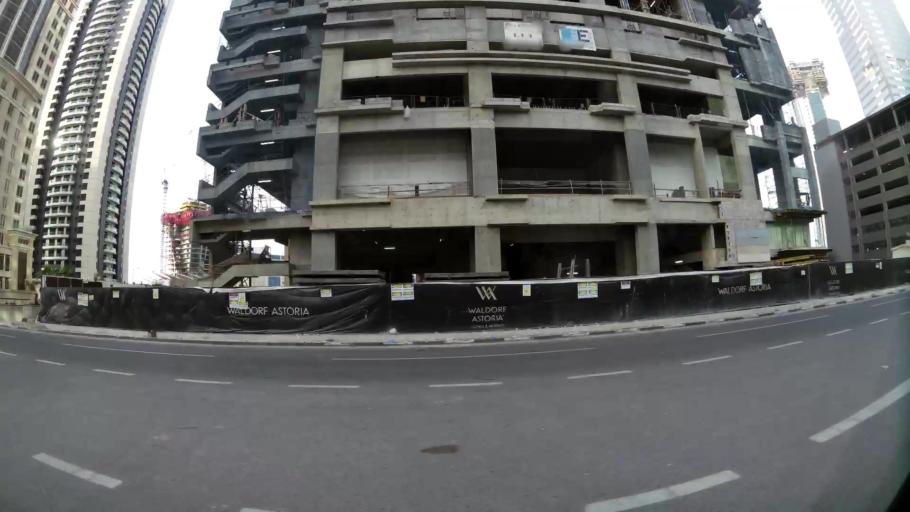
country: QA
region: Baladiyat ad Dawhah
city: Doha
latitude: 25.3269
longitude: 51.5329
